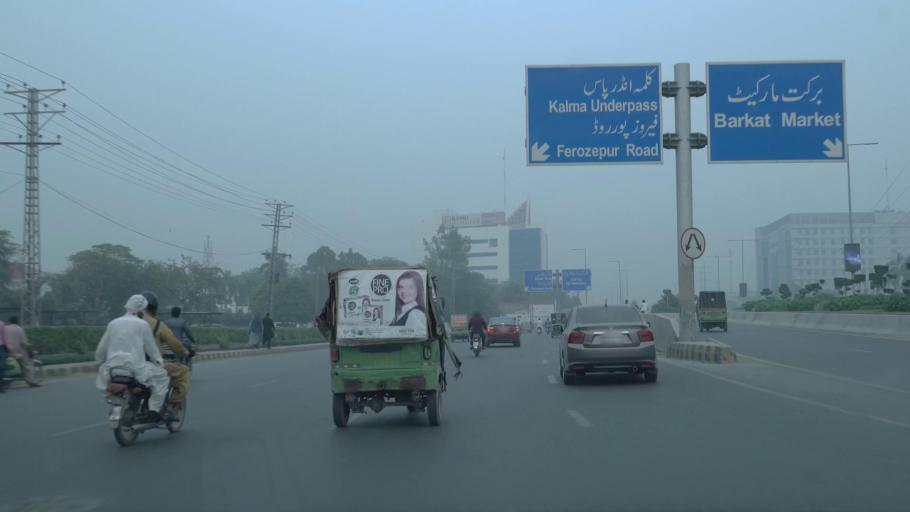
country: PK
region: Punjab
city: Lahore
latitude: 31.5028
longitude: 74.3259
